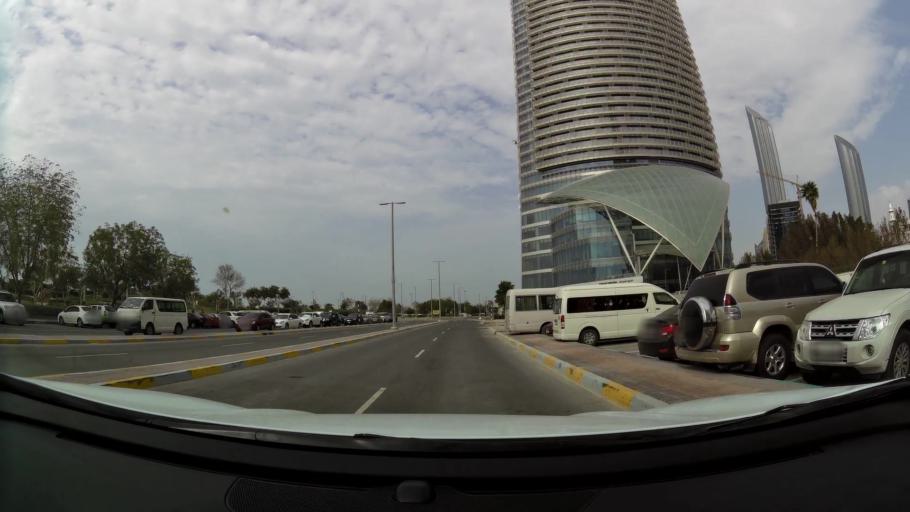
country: AE
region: Abu Dhabi
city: Abu Dhabi
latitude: 24.4839
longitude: 54.3499
